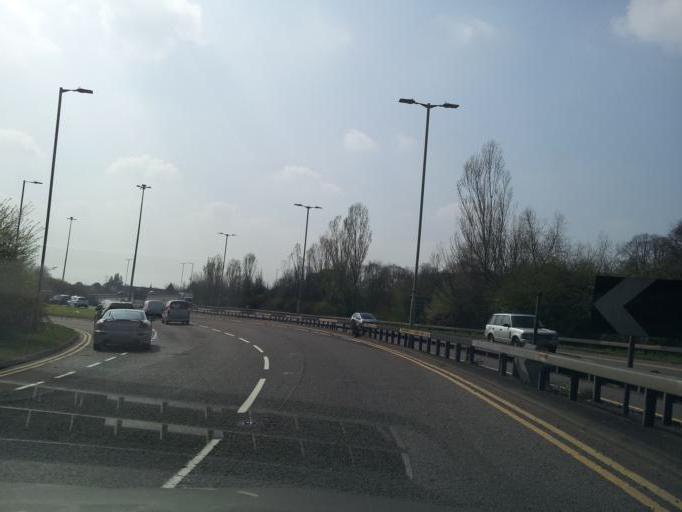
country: GB
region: England
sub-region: Hertfordshire
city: Watford
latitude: 51.6564
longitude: -0.3874
